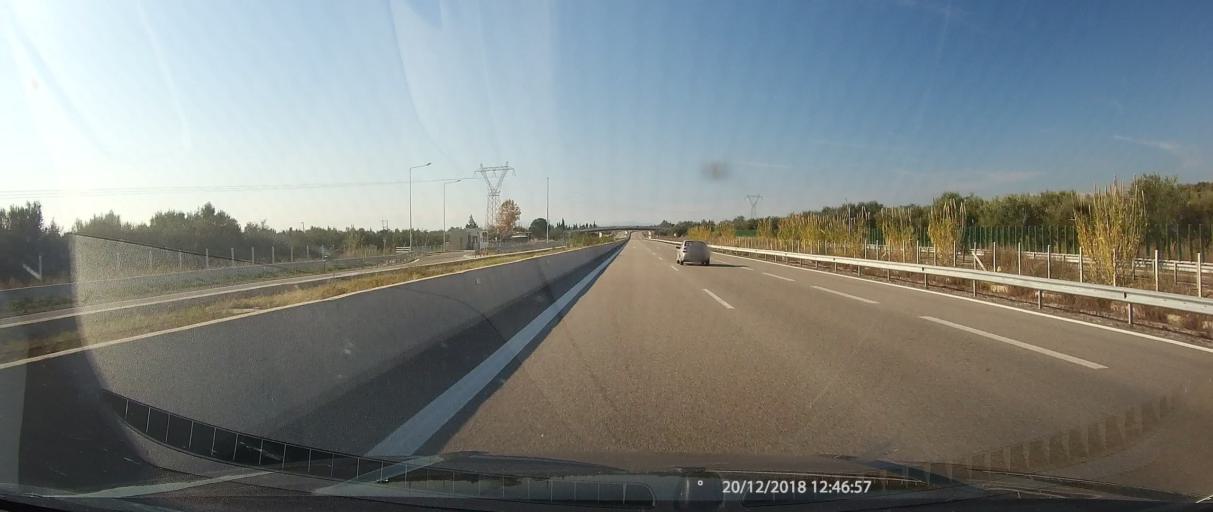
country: GR
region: West Greece
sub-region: Nomos Aitolias kai Akarnanias
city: Mesolongi
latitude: 38.3922
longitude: 21.4599
